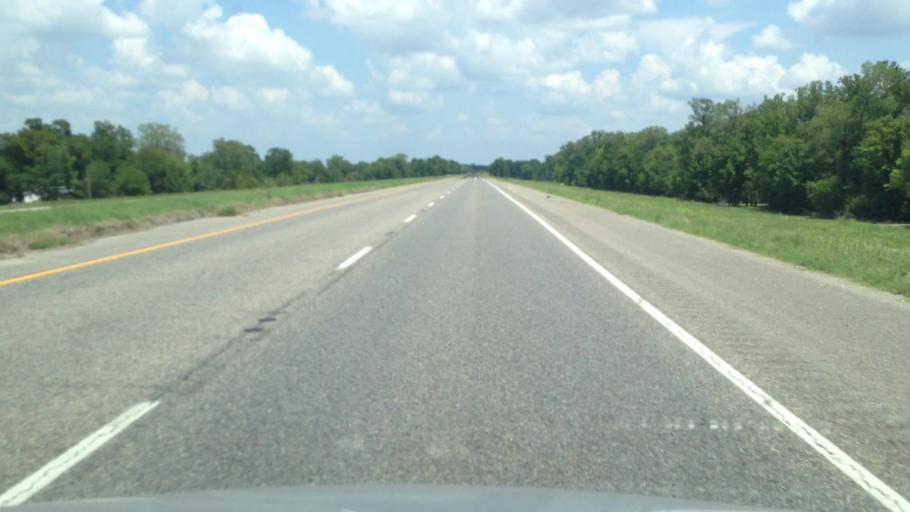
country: US
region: Louisiana
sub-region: Saint Landry Parish
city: Krotz Springs
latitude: 30.5487
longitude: -91.8451
